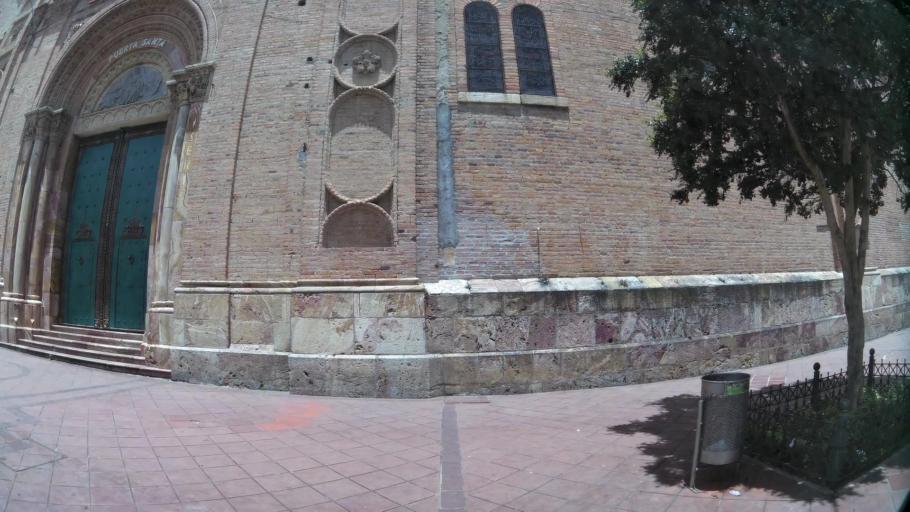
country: EC
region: Azuay
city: Cuenca
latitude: -2.8976
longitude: -79.0055
